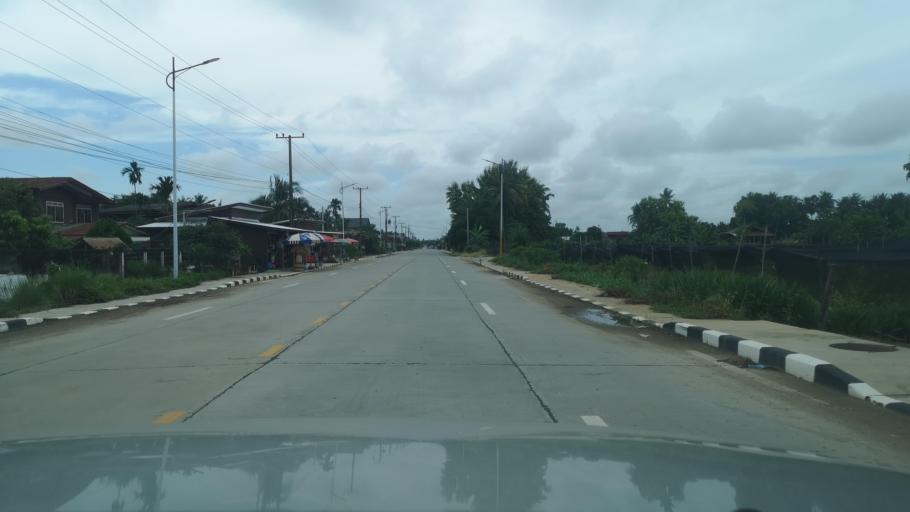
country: TH
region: Nong Khai
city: Tha Bo
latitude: 17.8203
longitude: 102.6641
